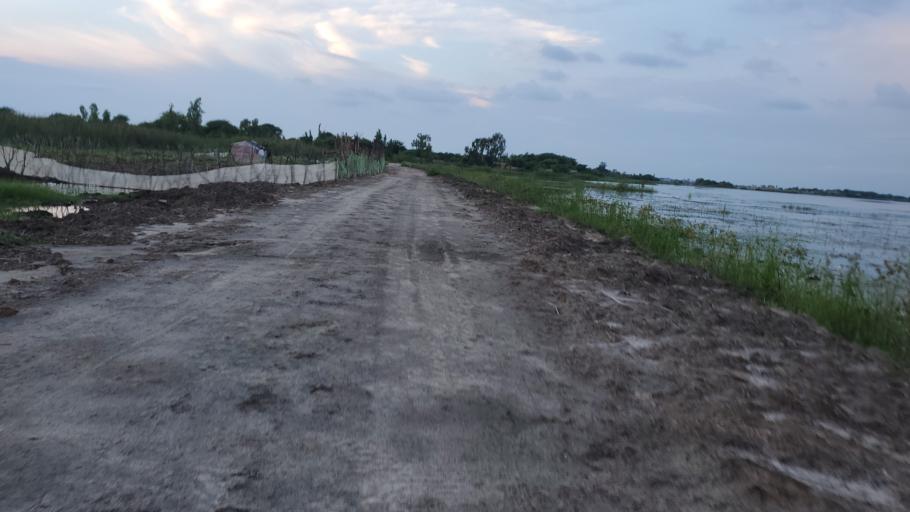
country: SN
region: Saint-Louis
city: Saint-Louis
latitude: 16.0358
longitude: -16.4167
